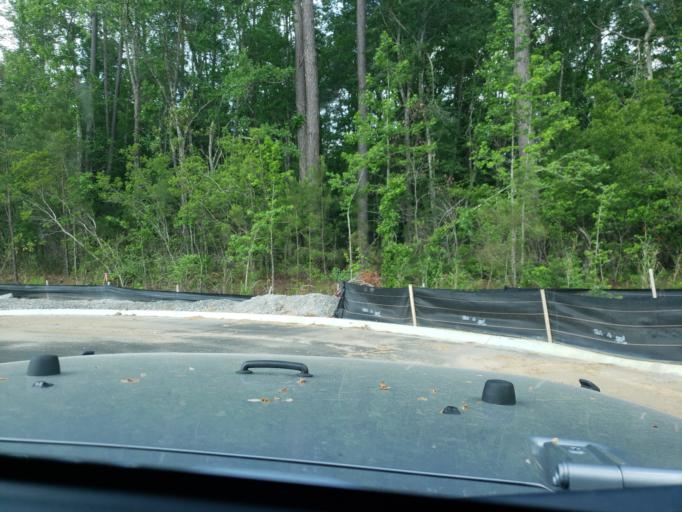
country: US
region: Georgia
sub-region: Chatham County
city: Georgetown
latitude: 32.0436
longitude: -81.2283
